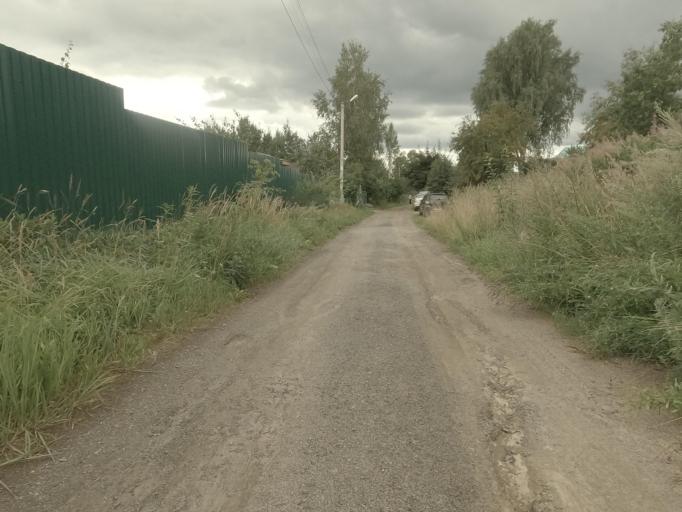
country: RU
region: Leningrad
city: Koltushi
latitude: 59.8879
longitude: 30.6951
